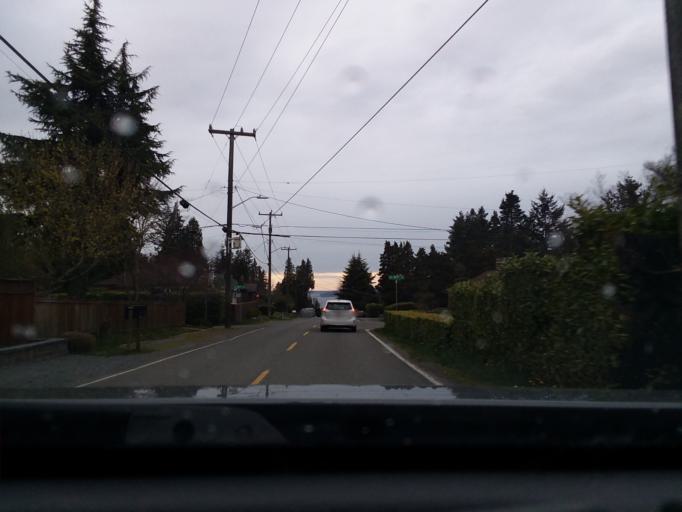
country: US
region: Washington
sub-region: King County
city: Shoreline
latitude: 47.6917
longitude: -122.3930
